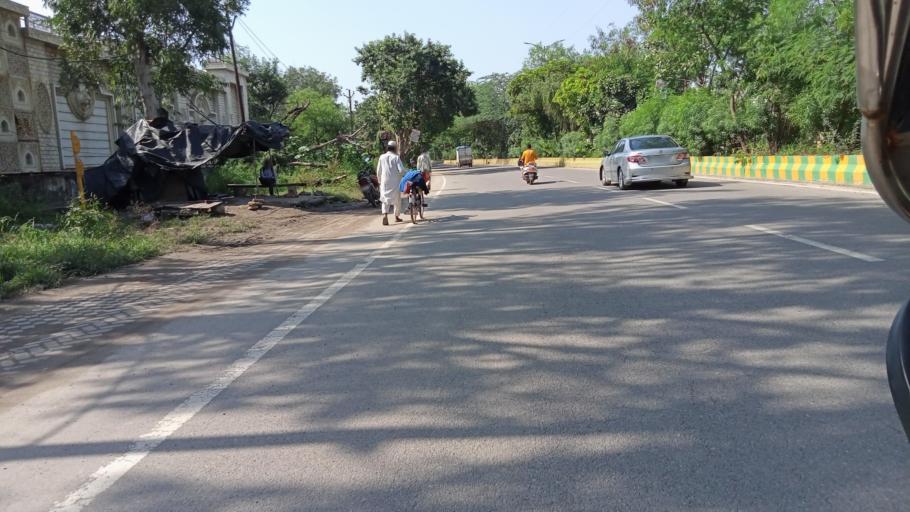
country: IN
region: Uttar Pradesh
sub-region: Ghaziabad
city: Ghaziabad
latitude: 28.6701
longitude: 77.3685
